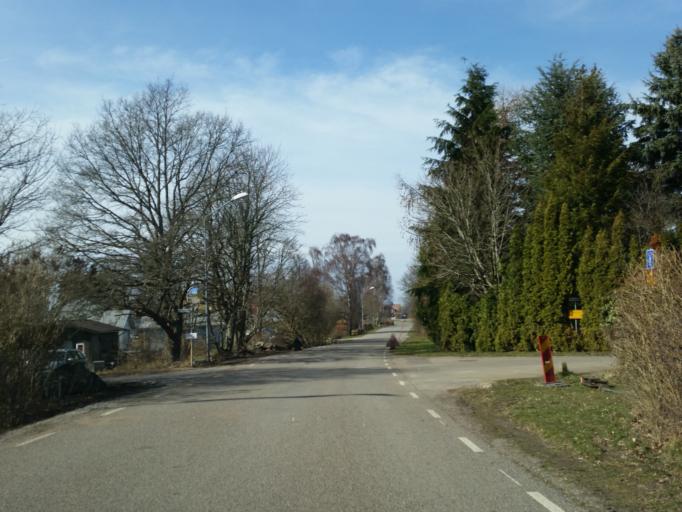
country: SE
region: Kalmar
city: Faerjestaden
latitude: 56.7558
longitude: 16.5331
